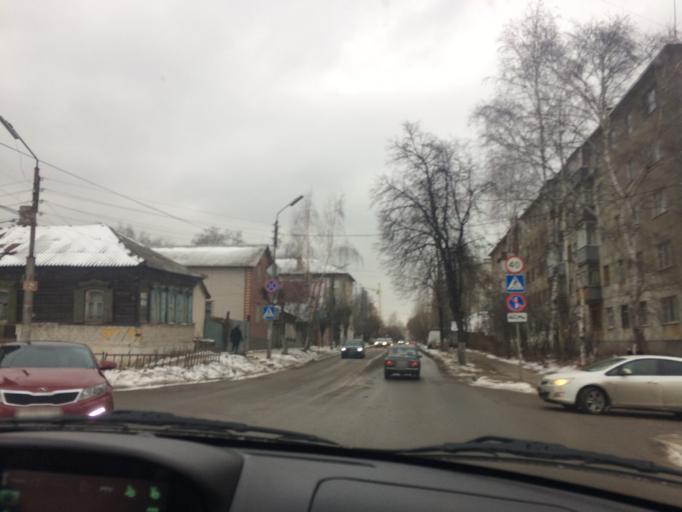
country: RU
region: Rjazan
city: Ryazan'
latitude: 54.6213
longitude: 39.7391
